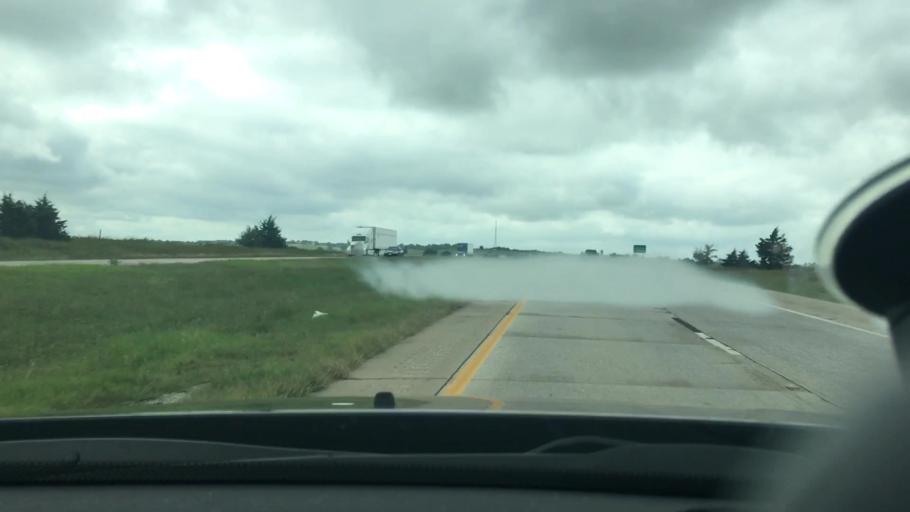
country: US
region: Oklahoma
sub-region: Bryan County
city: Durant
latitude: 34.1584
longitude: -96.2592
